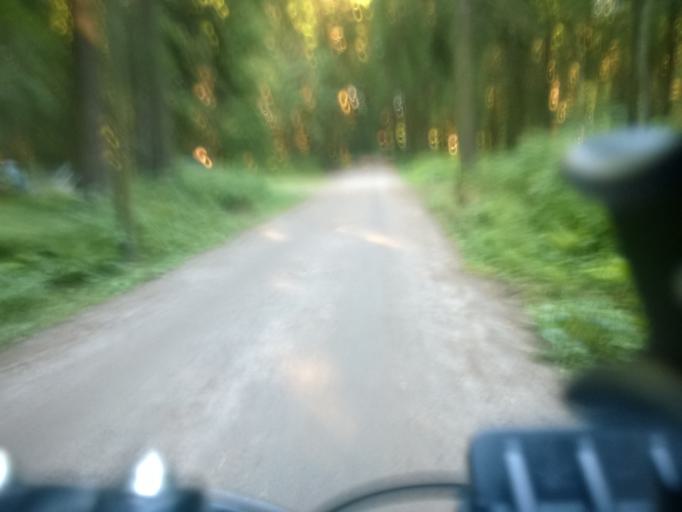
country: FI
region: Uusimaa
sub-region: Helsinki
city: Helsinki
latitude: 60.1989
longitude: 24.9180
